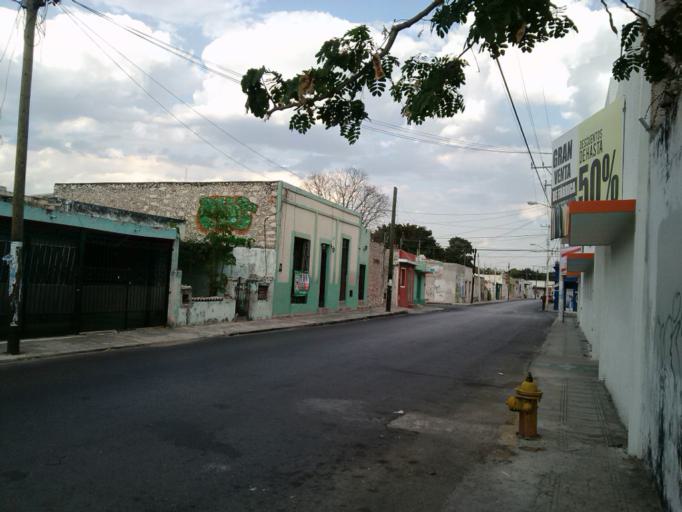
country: MX
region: Yucatan
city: Merida
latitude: 20.9643
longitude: -89.6125
